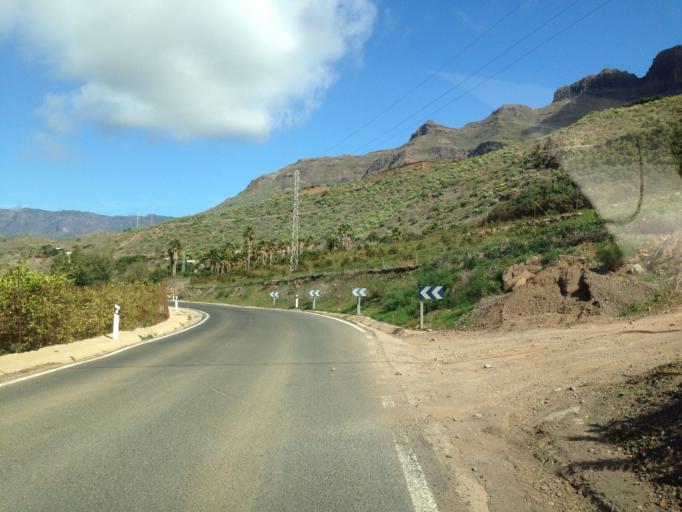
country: ES
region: Canary Islands
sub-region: Provincia de Las Palmas
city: Santa Lucia
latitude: 27.8664
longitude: -15.5648
